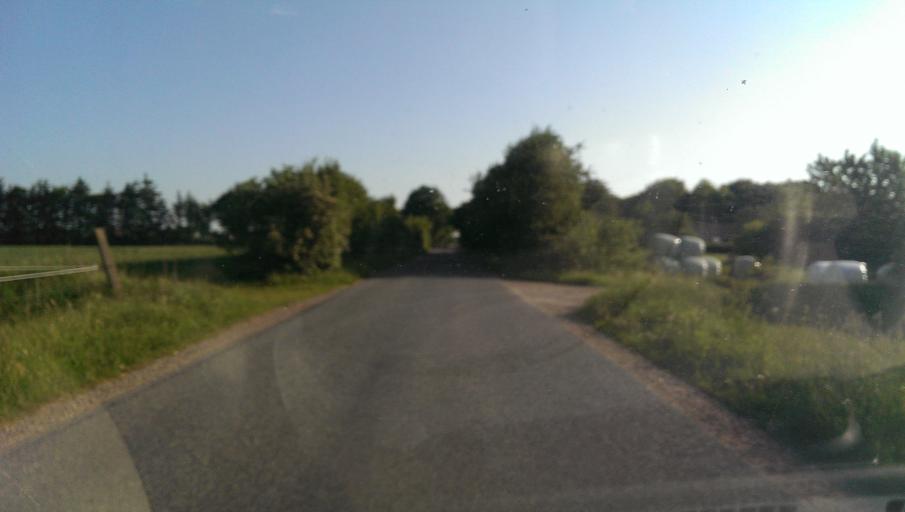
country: DK
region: South Denmark
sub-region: Esbjerg Kommune
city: Tjaereborg
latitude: 55.4706
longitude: 8.6145
